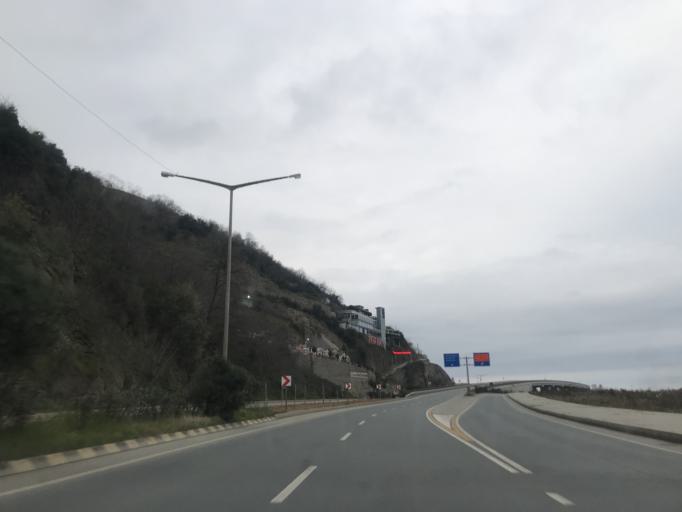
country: TR
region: Trabzon
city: Derecik
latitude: 40.9996
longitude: 39.6387
